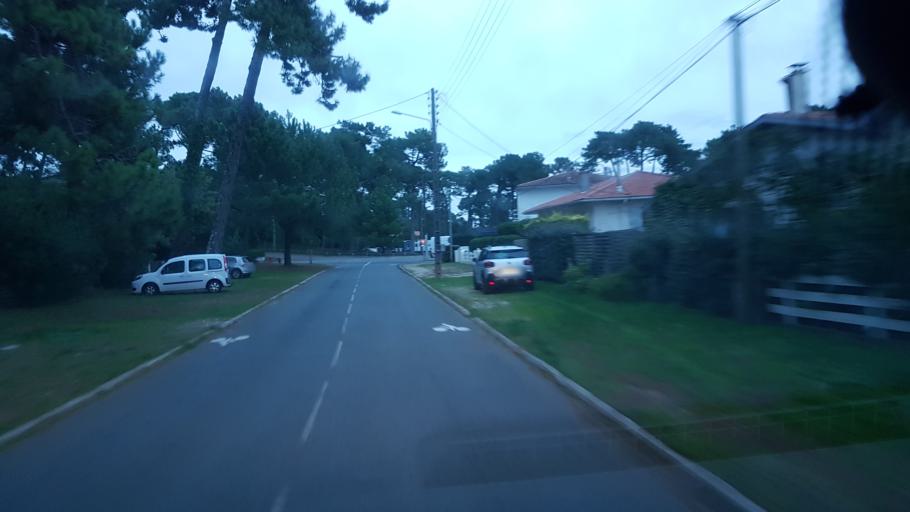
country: FR
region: Aquitaine
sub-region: Departement de la Gironde
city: Arcachon
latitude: 44.7037
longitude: -1.2286
